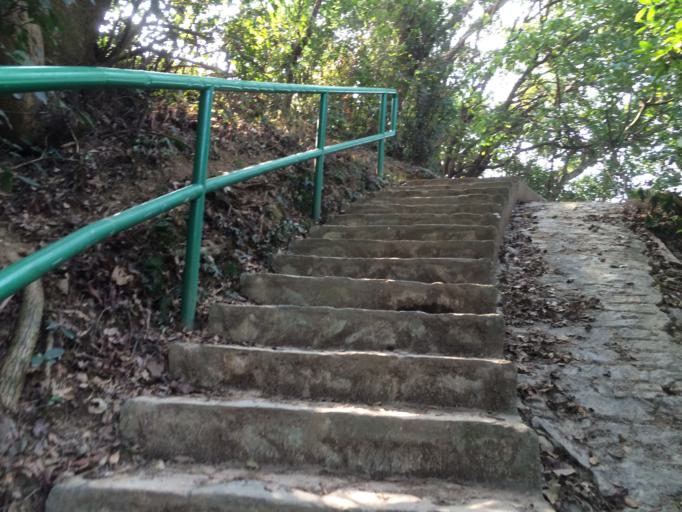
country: HK
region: Tai Po
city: Tai Po
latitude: 22.4539
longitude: 114.2145
